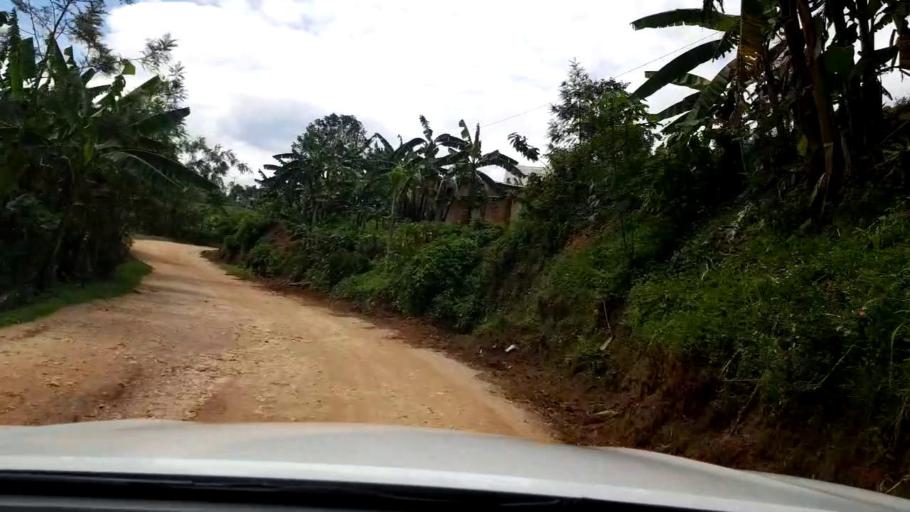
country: RW
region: Southern Province
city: Gitarama
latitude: -1.9252
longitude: 29.6532
